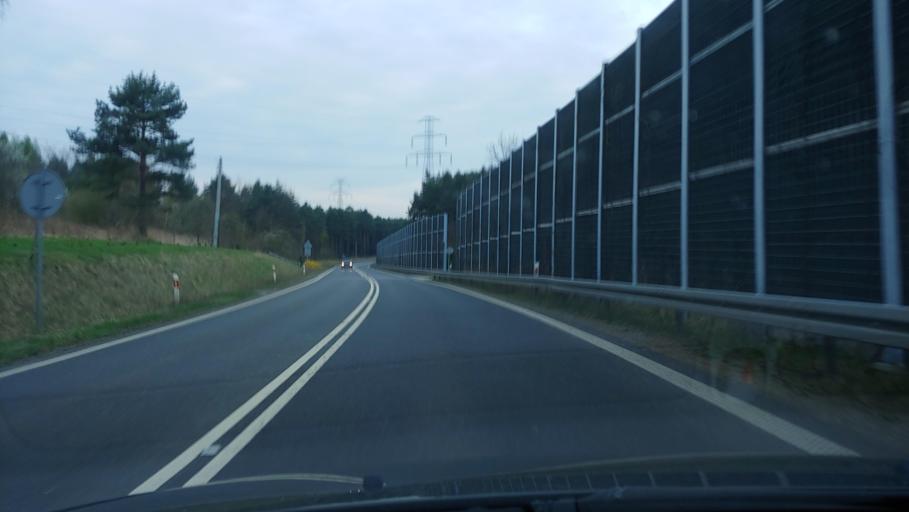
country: PL
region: Silesian Voivodeship
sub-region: Jaworzno
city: Jaworzno
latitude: 50.1729
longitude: 19.2900
